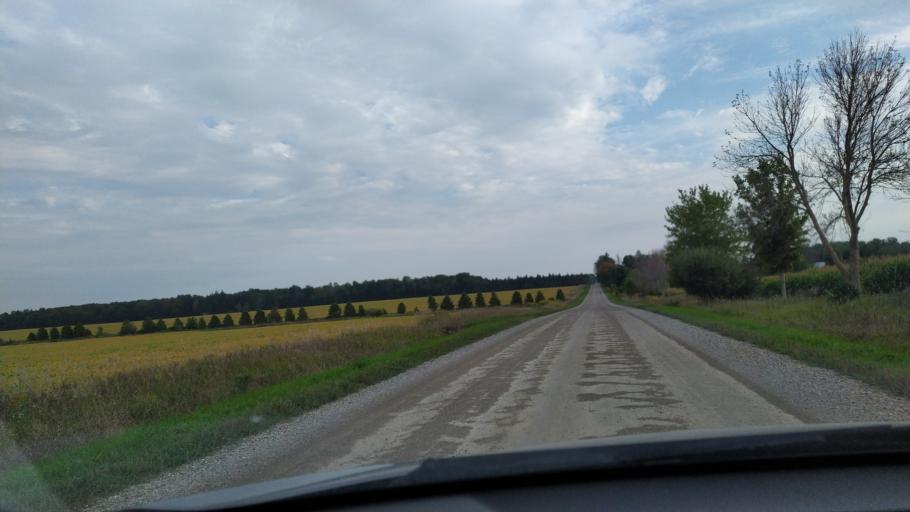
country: CA
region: Ontario
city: Stratford
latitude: 43.4137
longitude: -80.9131
